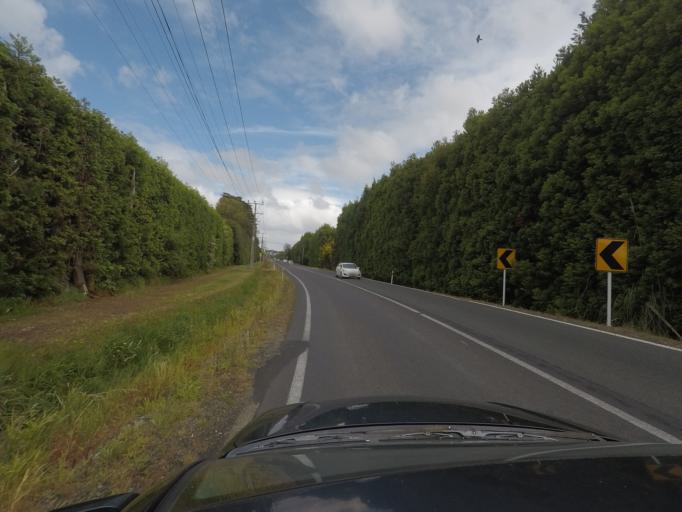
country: NZ
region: Auckland
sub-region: Auckland
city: Muriwai Beach
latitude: -36.7733
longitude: 174.5739
